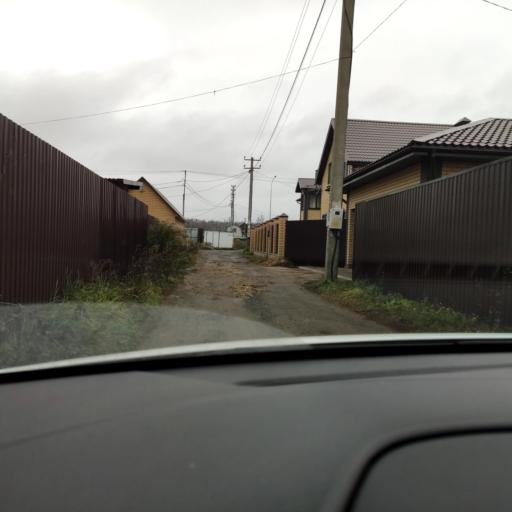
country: RU
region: Tatarstan
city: Stolbishchi
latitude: 55.6928
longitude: 49.2139
